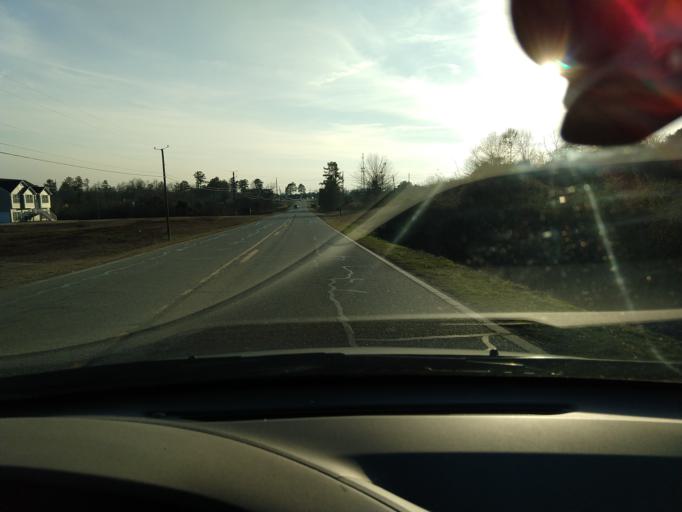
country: US
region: Georgia
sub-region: Sumter County
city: Americus
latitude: 32.0780
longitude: -84.2136
